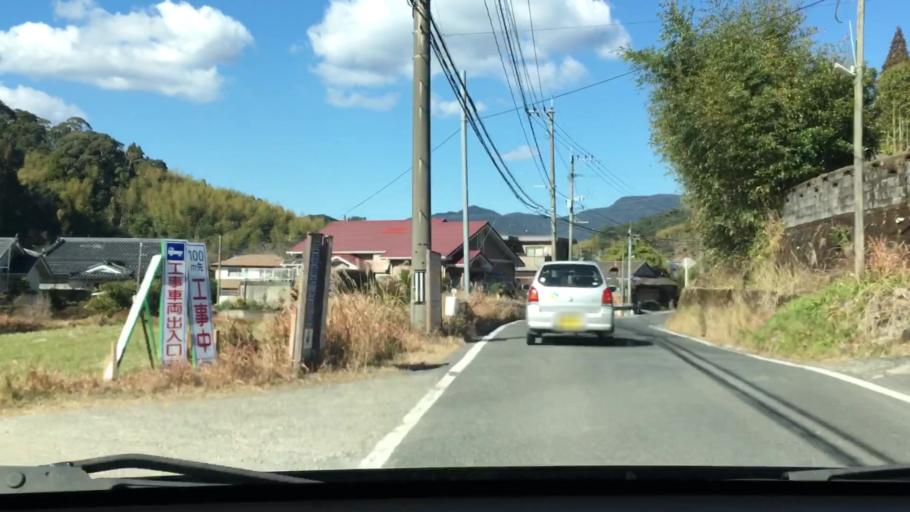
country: JP
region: Kagoshima
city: Ijuin
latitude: 31.6852
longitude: 130.4686
